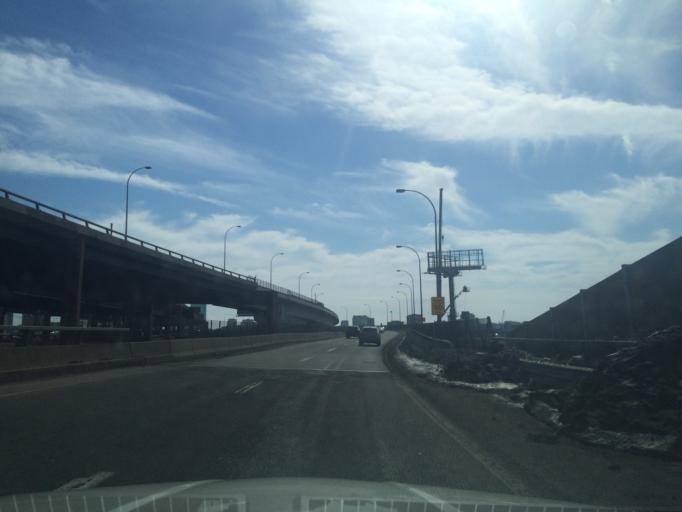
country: US
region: Massachusetts
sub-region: Middlesex County
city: Somerville
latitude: 42.3826
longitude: -71.0769
